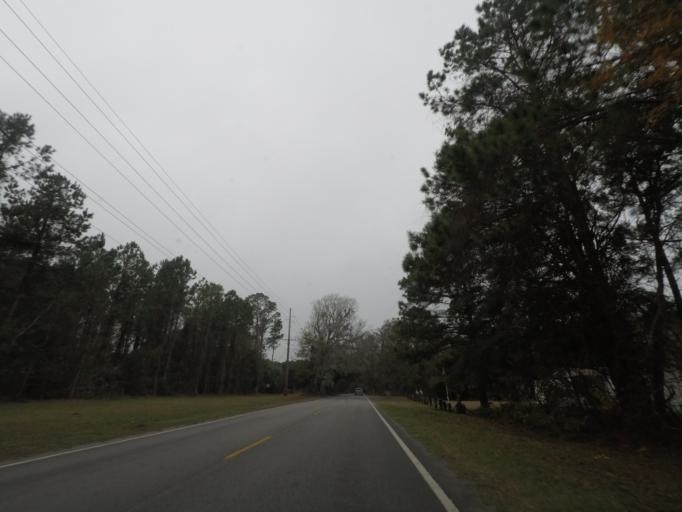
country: US
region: South Carolina
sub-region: Charleston County
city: Seabrook Island
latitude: 32.5813
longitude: -80.3356
